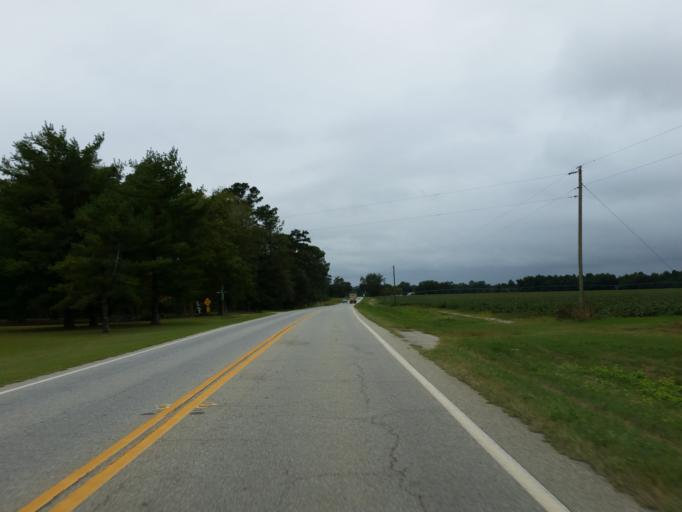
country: US
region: Georgia
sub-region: Cook County
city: Adel
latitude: 31.1330
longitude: -83.3748
